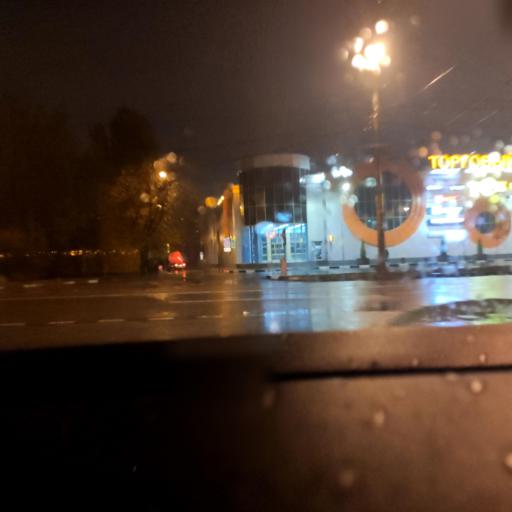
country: RU
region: Voronezj
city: Podgornoye
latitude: 51.7072
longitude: 39.1475
